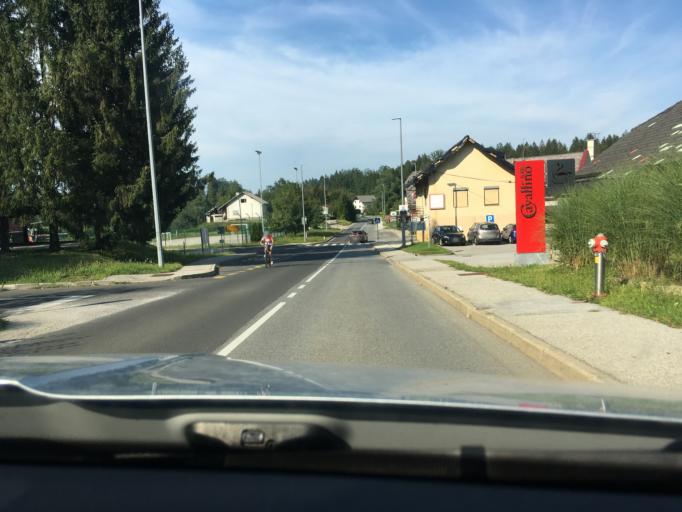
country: SI
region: Crnomelj
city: Crnomelj
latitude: 45.5605
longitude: 15.1691
